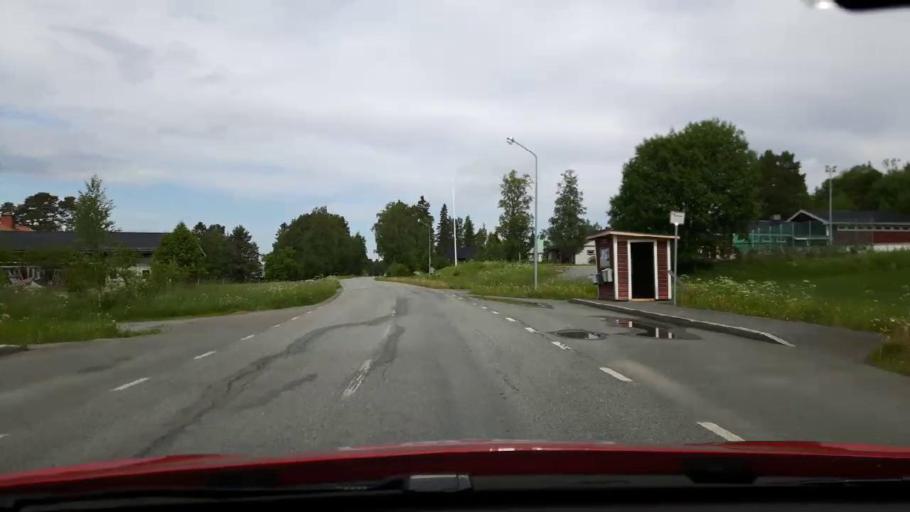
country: SE
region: Jaemtland
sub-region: OEstersunds Kommun
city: Ostersund
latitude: 63.0360
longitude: 14.4684
